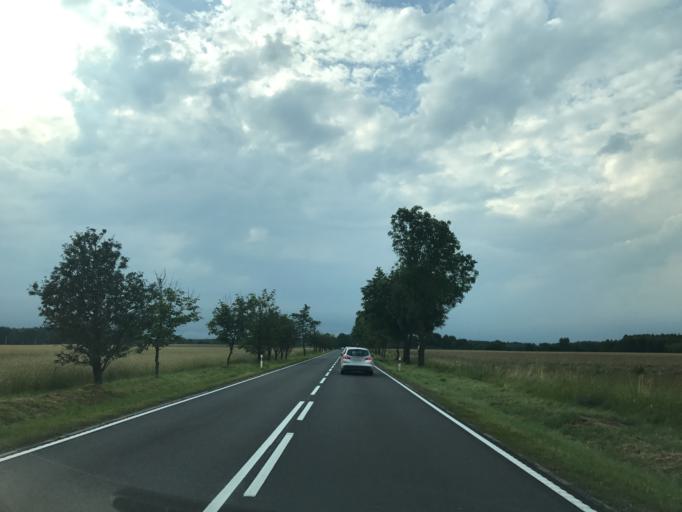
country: PL
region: Pomeranian Voivodeship
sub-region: Powiat czluchowski
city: Rzeczenica
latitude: 53.7430
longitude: 17.1774
